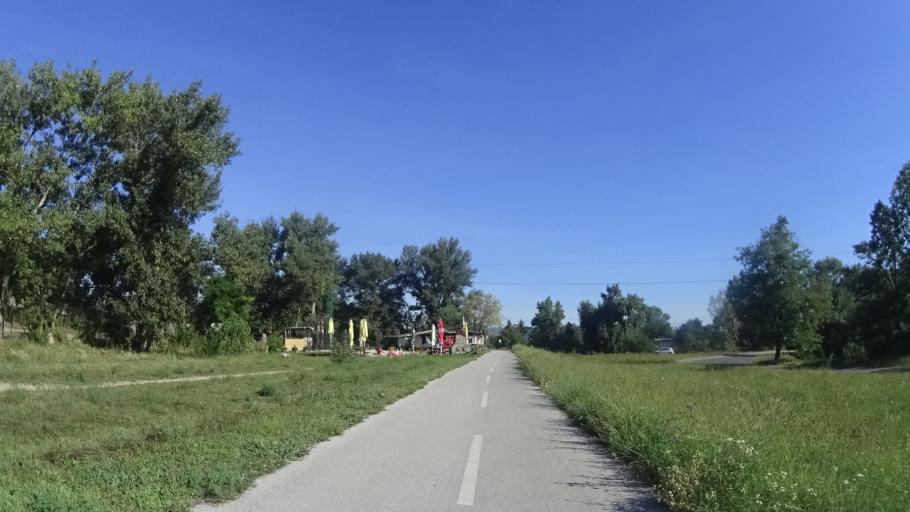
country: SK
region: Bratislavsky
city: Bratislava
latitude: 48.1290
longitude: 17.1587
